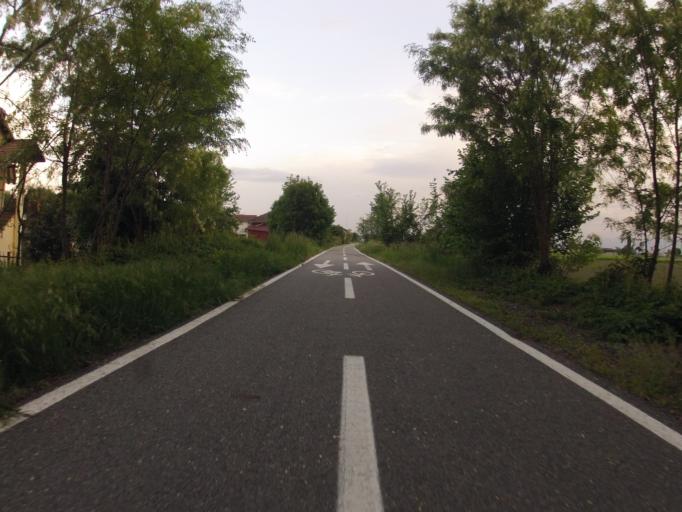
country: IT
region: Piedmont
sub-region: Provincia di Torino
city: Vigone
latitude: 44.8383
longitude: 7.4911
